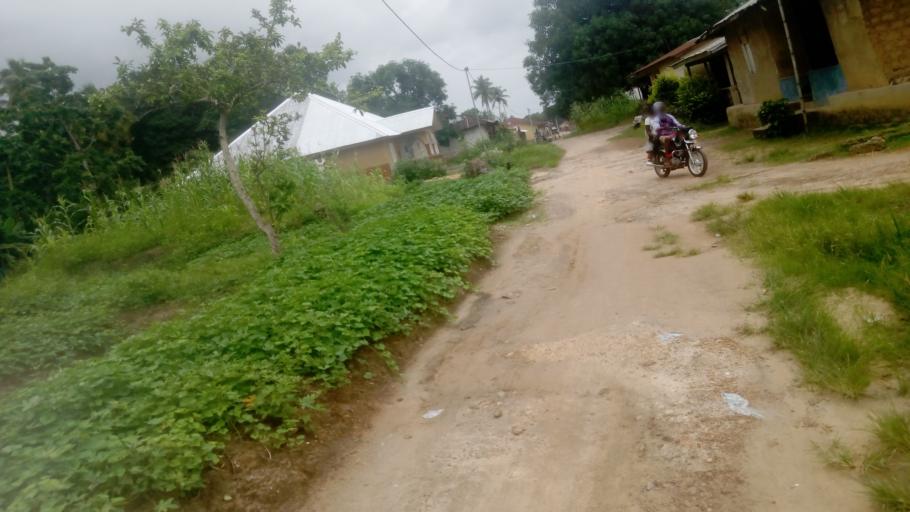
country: SL
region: Northern Province
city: Lunsar
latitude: 8.6789
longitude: -12.5353
